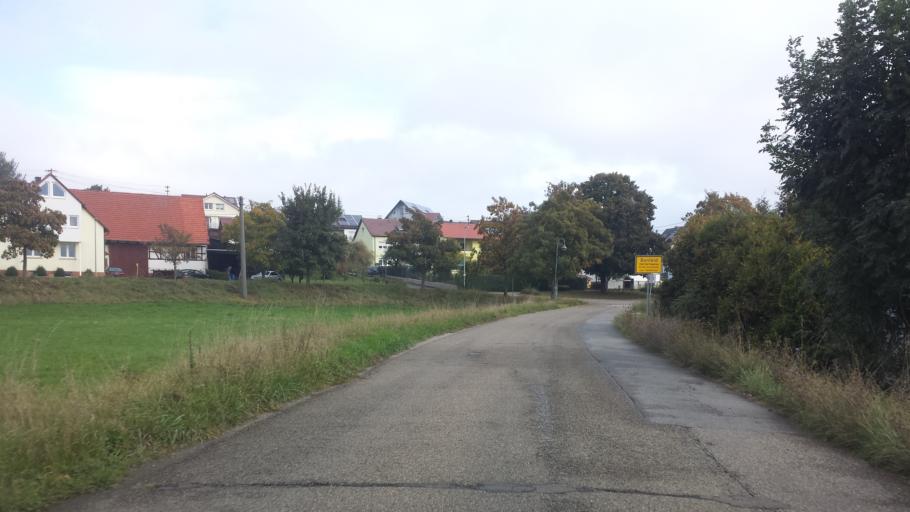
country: DE
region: Baden-Wuerttemberg
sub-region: Regierungsbezirk Stuttgart
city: Bad Rappenau
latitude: 49.2137
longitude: 9.0888
